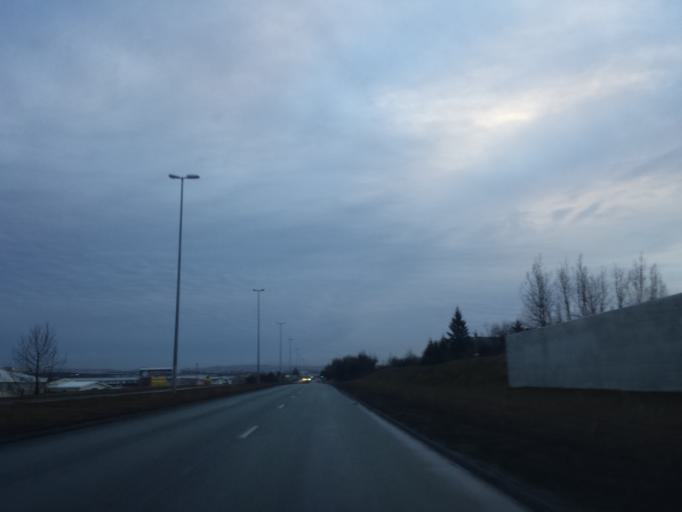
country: IS
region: Capital Region
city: Reykjavik
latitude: 64.1396
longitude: -21.8506
